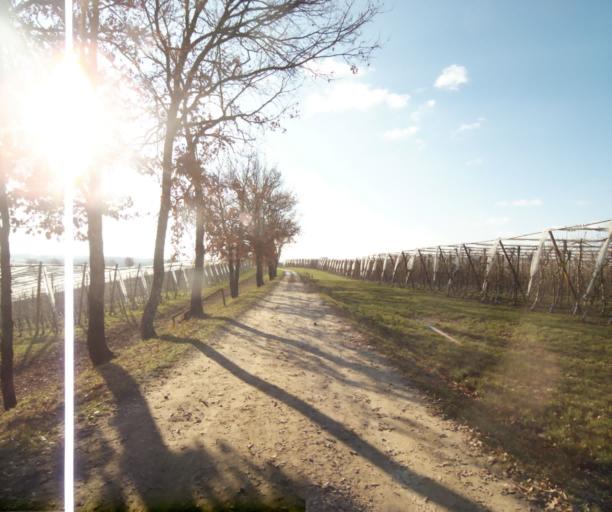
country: FR
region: Midi-Pyrenees
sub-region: Departement du Tarn-et-Garonne
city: Moissac
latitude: 44.1390
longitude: 1.0506
